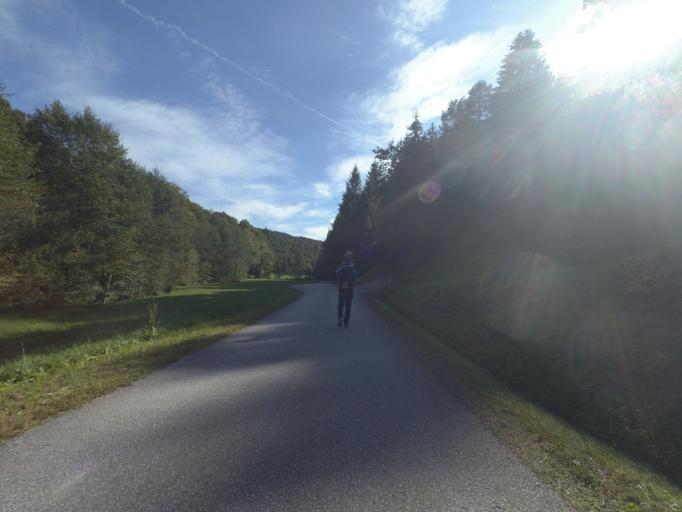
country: AT
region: Styria
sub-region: Politischer Bezirk Leibnitz
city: Kitzeck im Sausal
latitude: 46.7715
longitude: 15.4413
